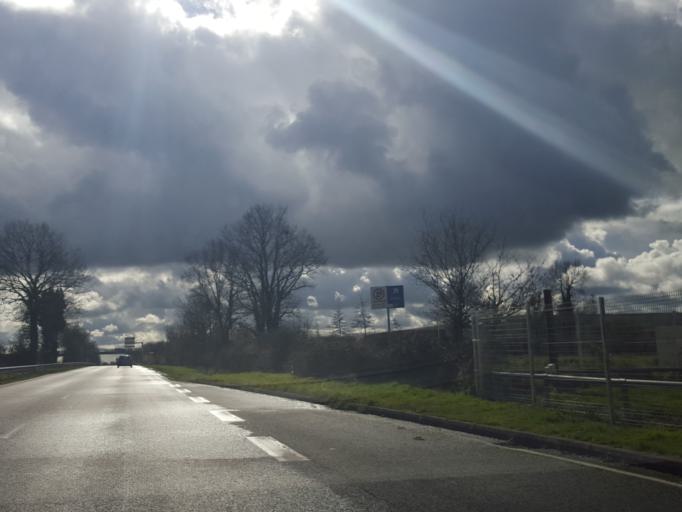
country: FR
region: Pays de la Loire
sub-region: Departement de la Vendee
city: Belleville-sur-Vie
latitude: 46.7482
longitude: -1.4306
